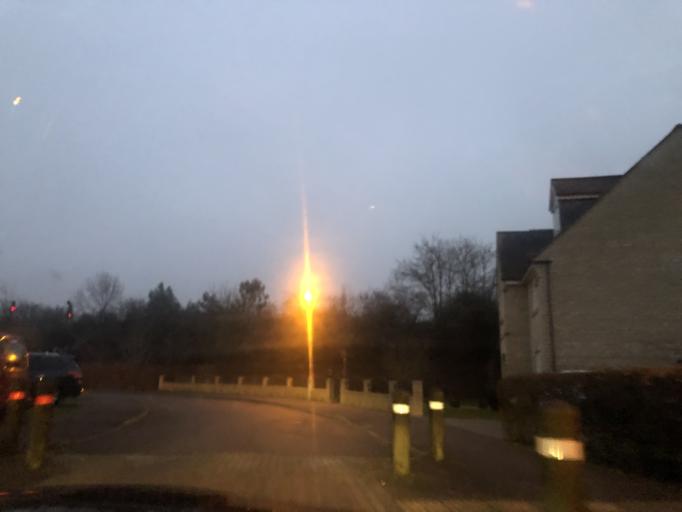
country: GB
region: England
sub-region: Oxfordshire
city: Bicester
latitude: 51.9099
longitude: -1.1660
